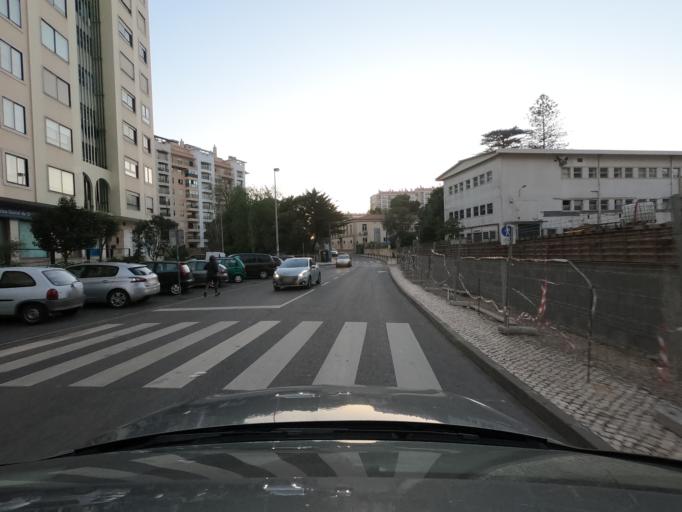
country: PT
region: Lisbon
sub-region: Sintra
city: Cacem
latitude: 38.7570
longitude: -9.2778
